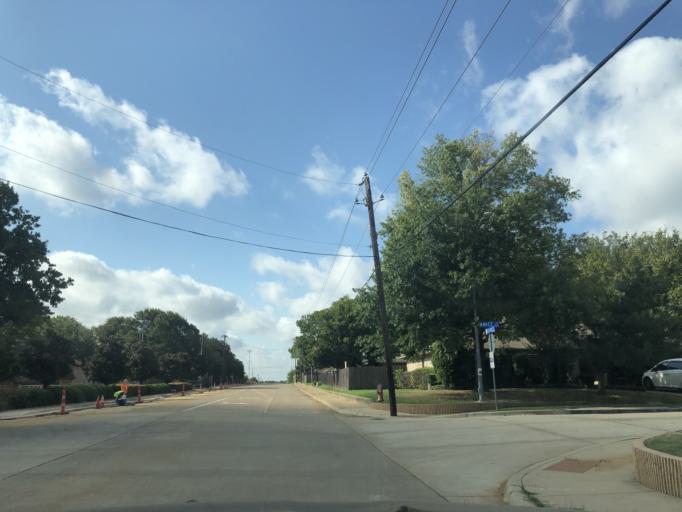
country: US
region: Texas
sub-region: Tarrant County
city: Euless
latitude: 32.8747
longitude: -97.0738
